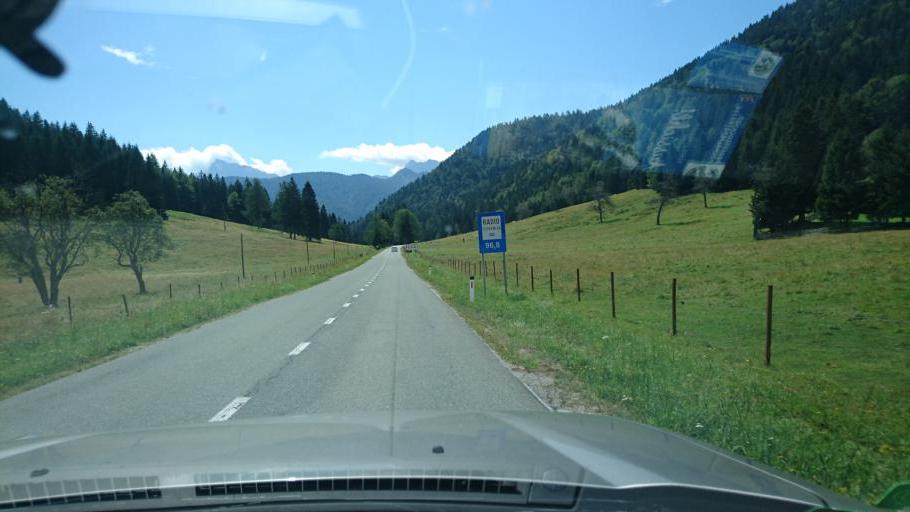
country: AT
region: Carinthia
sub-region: Politischer Bezirk Villach Land
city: Arnoldstein
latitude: 46.5149
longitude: 13.7510
